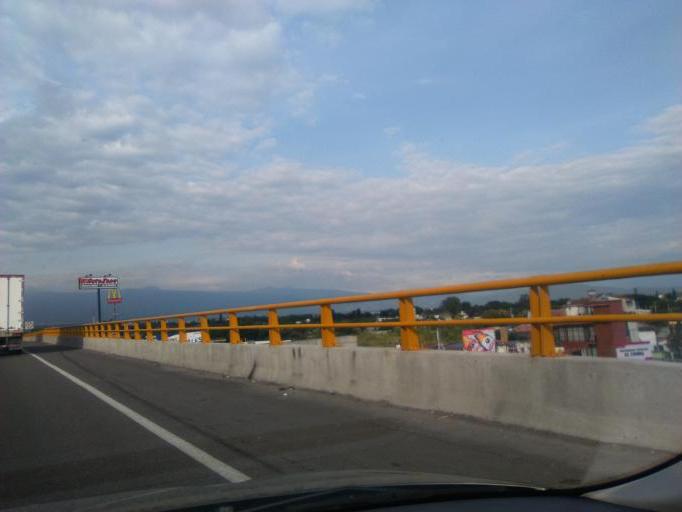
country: MX
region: Morelos
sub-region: Emiliano Zapata
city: Tres de Mayo
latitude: 18.8884
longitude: -99.2287
